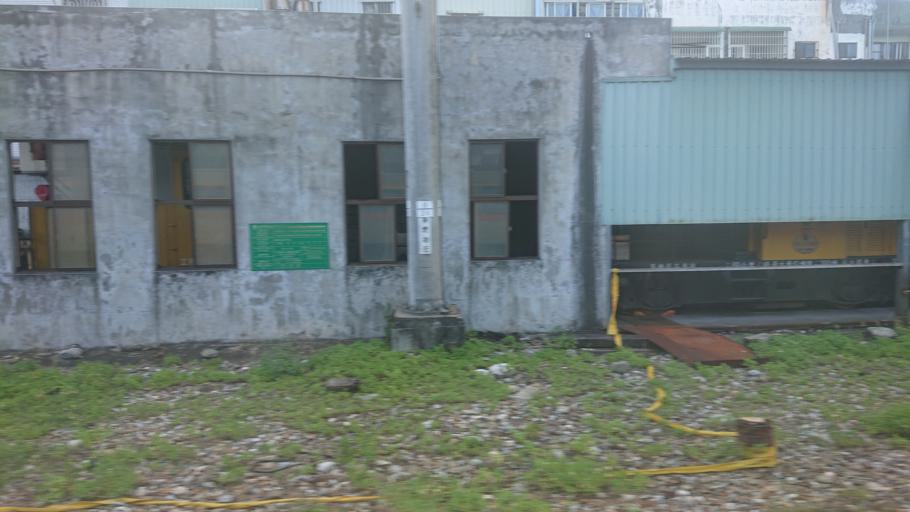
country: TW
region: Taiwan
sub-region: Hualien
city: Hualian
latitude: 23.9892
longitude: 121.5991
